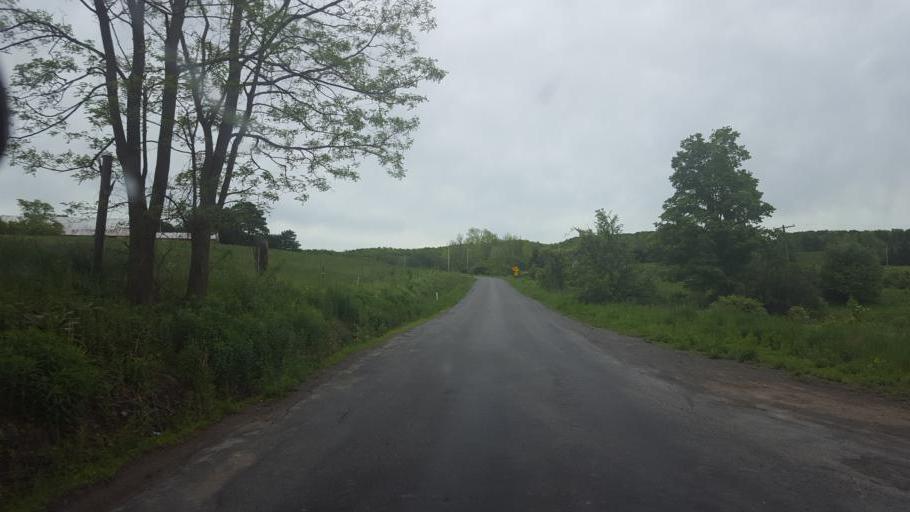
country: US
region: New York
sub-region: Herkimer County
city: Mohawk
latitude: 42.9539
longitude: -75.0249
